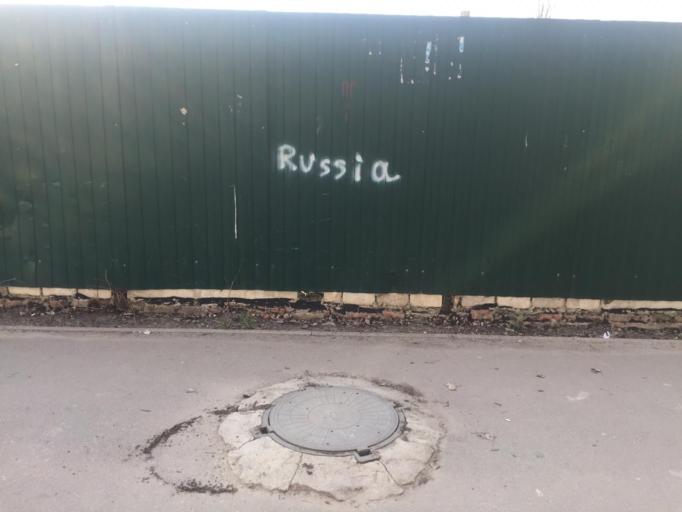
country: RU
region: Voronezj
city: Voronezh
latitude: 51.6782
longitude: 39.1447
